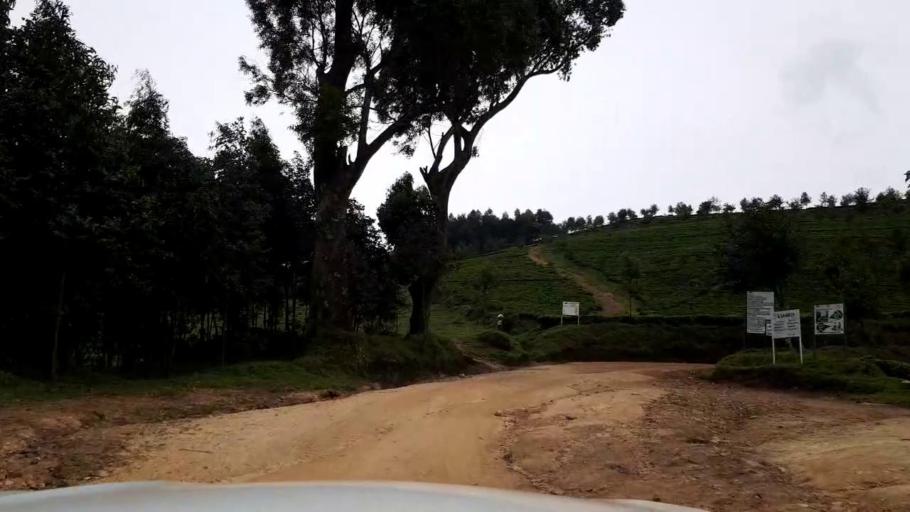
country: RW
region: Western Province
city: Kibuye
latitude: -1.9583
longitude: 29.4012
